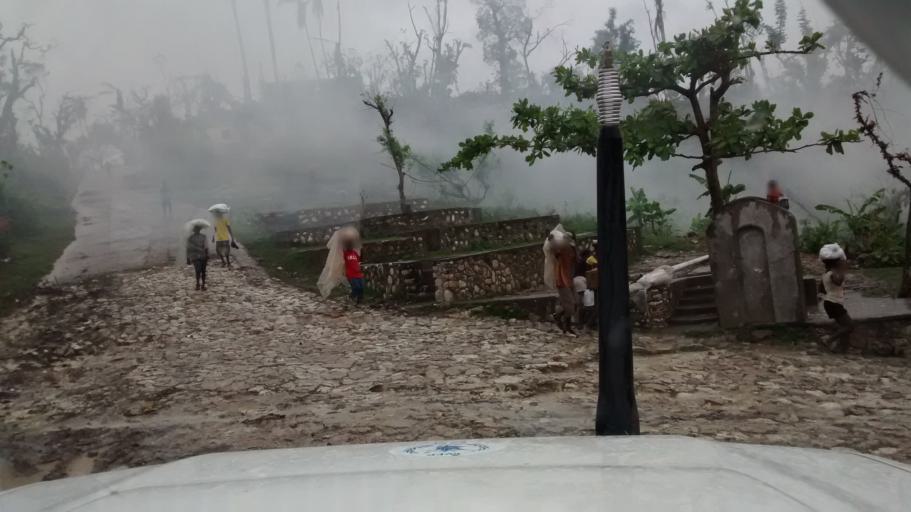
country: HT
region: Grandans
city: Moron
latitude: 18.5372
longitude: -74.1578
